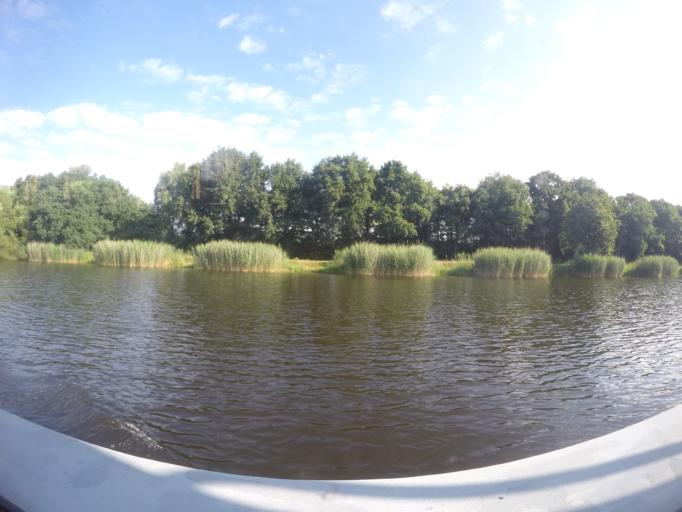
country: NL
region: Overijssel
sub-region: Gemeente Almelo
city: Almelo
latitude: 52.3692
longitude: 6.6311
